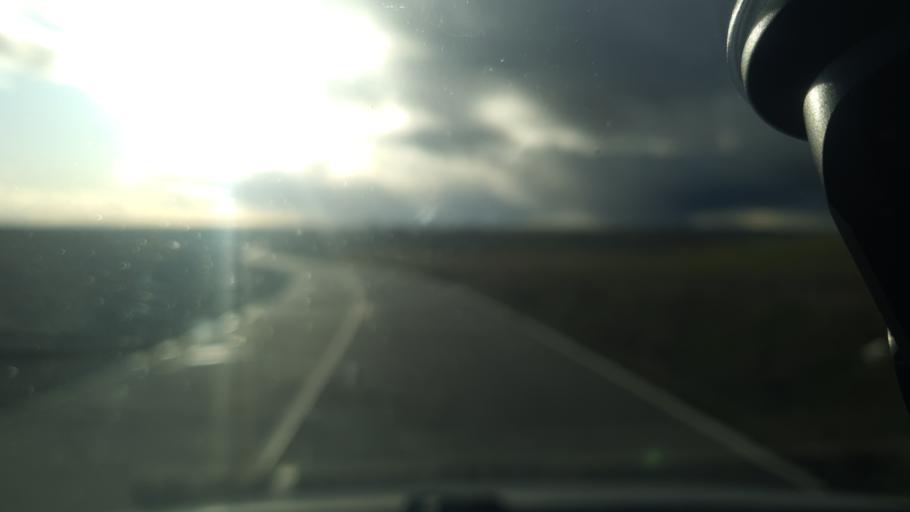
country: ES
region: Castille and Leon
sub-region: Provincia de Segovia
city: San Cristobal de la Vega
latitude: 41.1240
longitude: -4.6127
